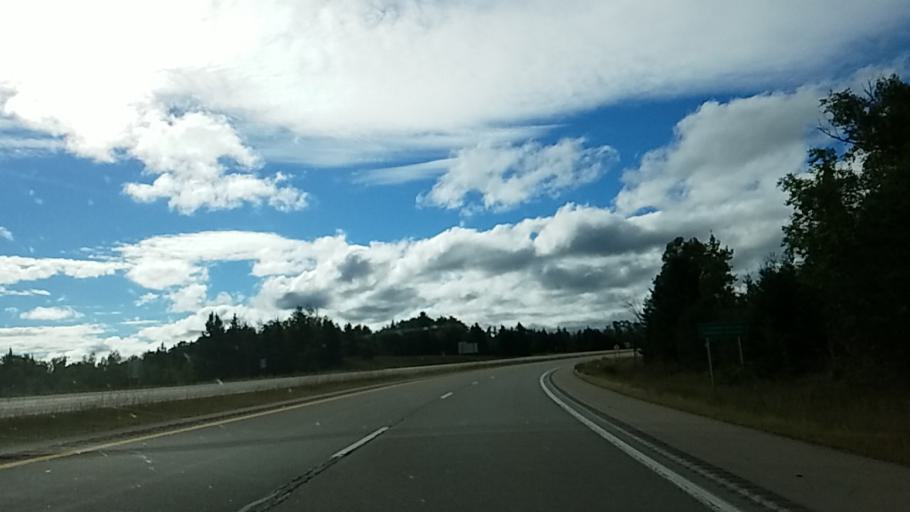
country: US
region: Michigan
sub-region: Mackinac County
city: Saint Ignace
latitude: 45.7621
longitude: -84.7313
